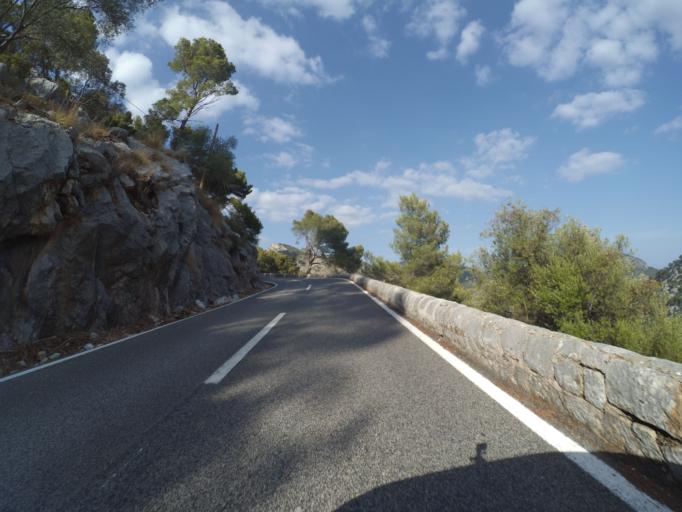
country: ES
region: Balearic Islands
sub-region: Illes Balears
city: Escorca
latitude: 39.7952
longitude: 2.8960
